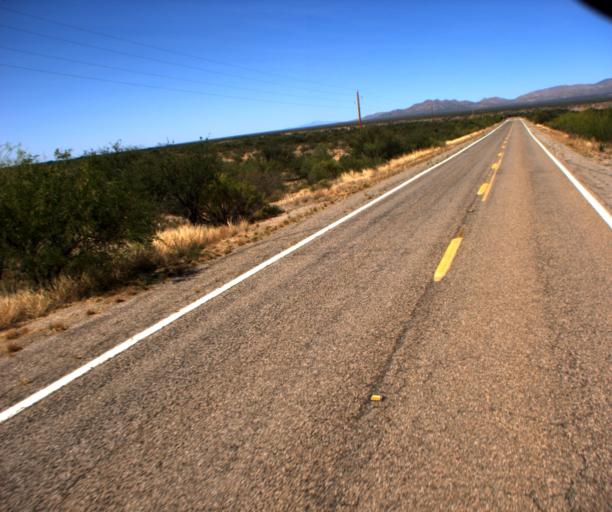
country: US
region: Arizona
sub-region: Pima County
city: Three Points
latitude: 31.8370
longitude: -111.4081
